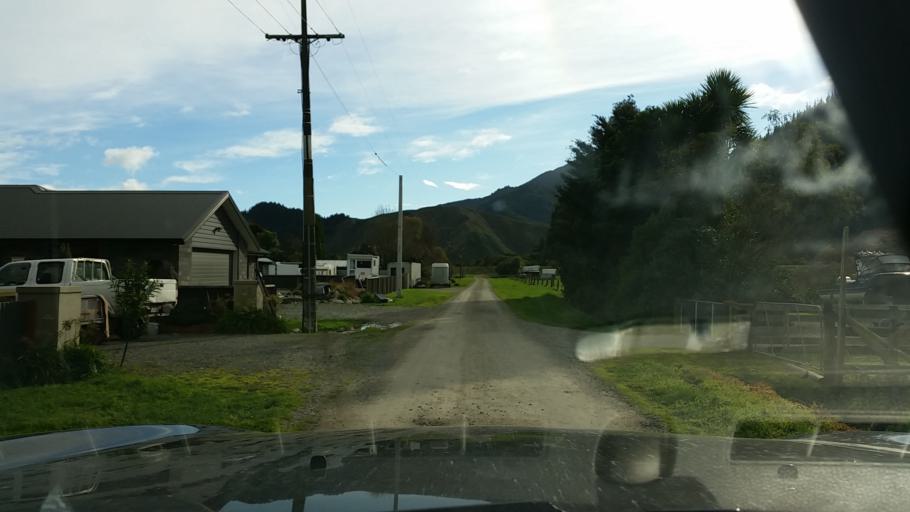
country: NZ
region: Marlborough
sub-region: Marlborough District
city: Blenheim
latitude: -41.4266
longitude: 173.9574
